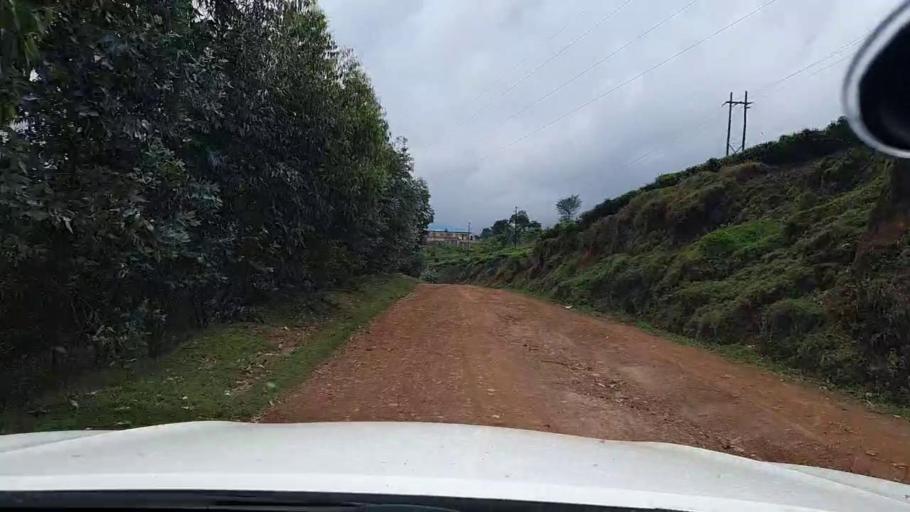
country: RW
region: Western Province
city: Kibuye
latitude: -2.1720
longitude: 29.4344
